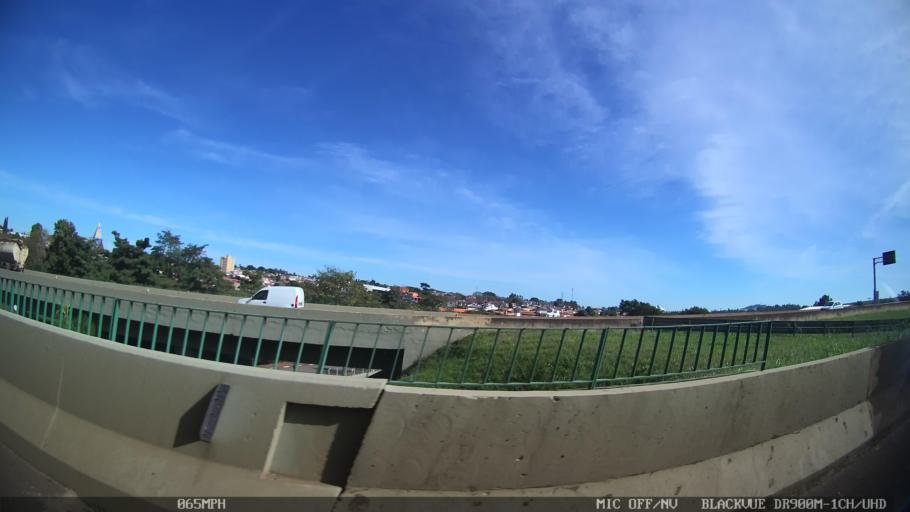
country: BR
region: Sao Paulo
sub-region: Araras
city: Araras
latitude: -22.3488
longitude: -47.3945
